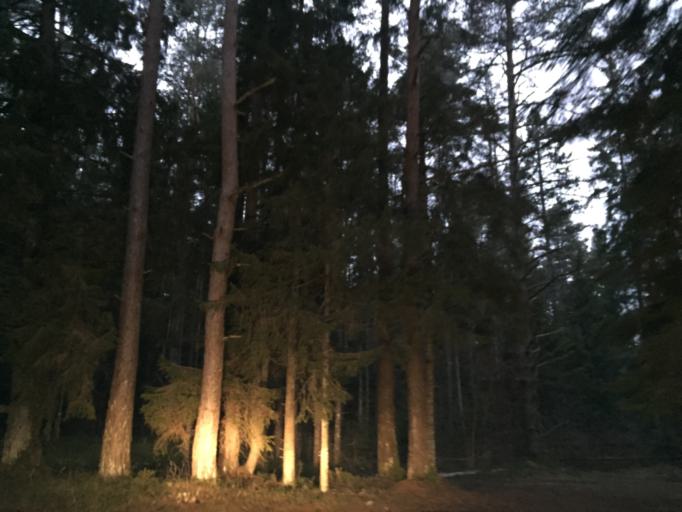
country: EE
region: Saare
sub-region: Kuressaare linn
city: Kuressaare
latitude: 58.5966
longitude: 22.6092
